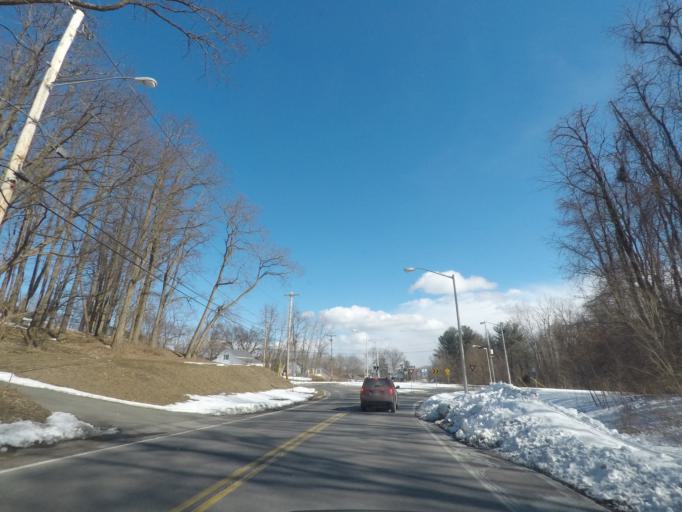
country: US
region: New York
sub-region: Albany County
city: McKownville
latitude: 42.6645
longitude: -73.8488
